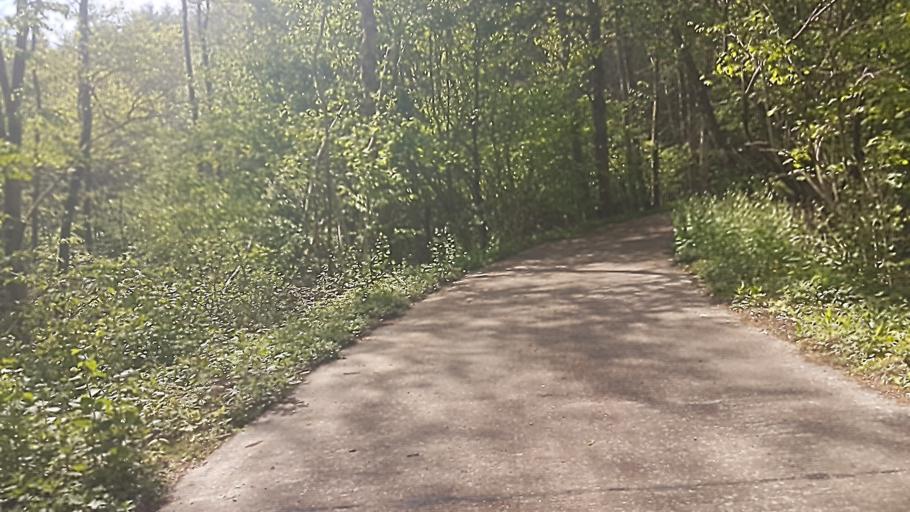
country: BE
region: Wallonia
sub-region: Province de Namur
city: Couvin
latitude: 50.0456
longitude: 4.5952
